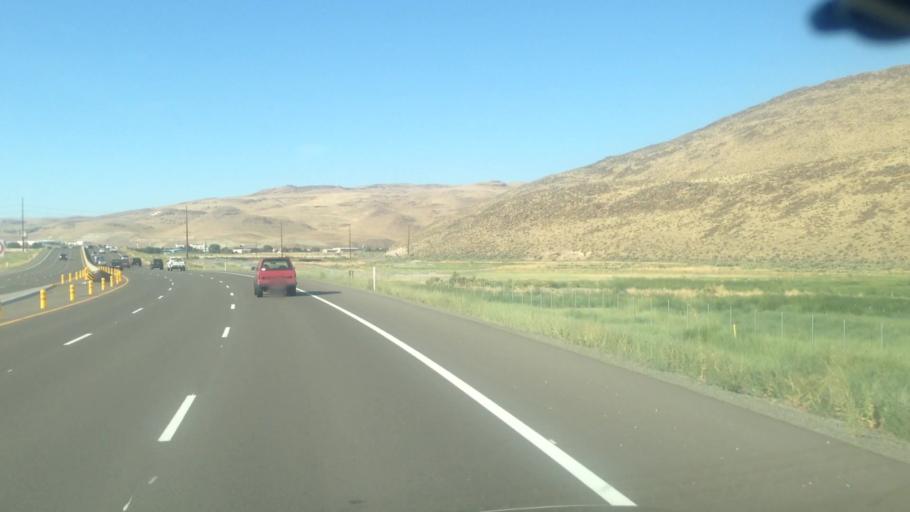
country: US
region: Nevada
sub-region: Washoe County
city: Sparks
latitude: 39.5091
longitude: -119.7161
